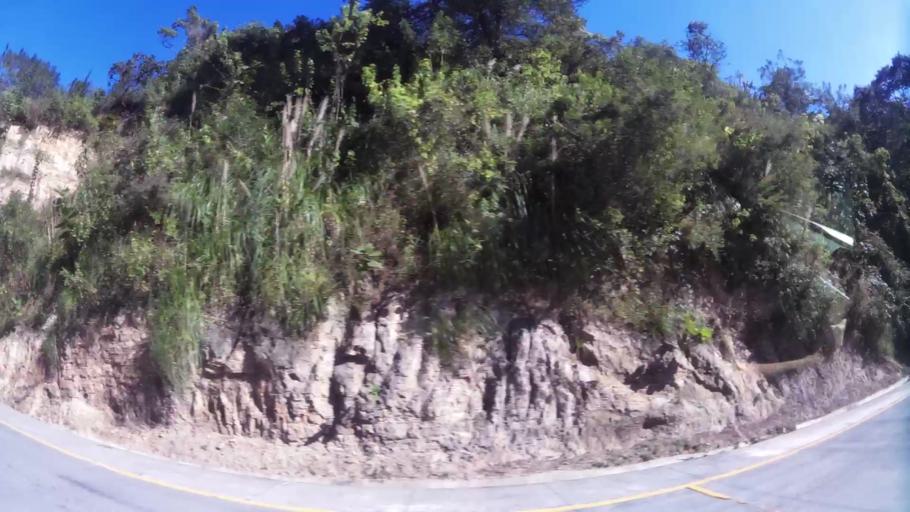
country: GT
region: Sacatepequez
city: Santa Lucia Milpas Altas
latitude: 14.5685
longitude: -90.6922
